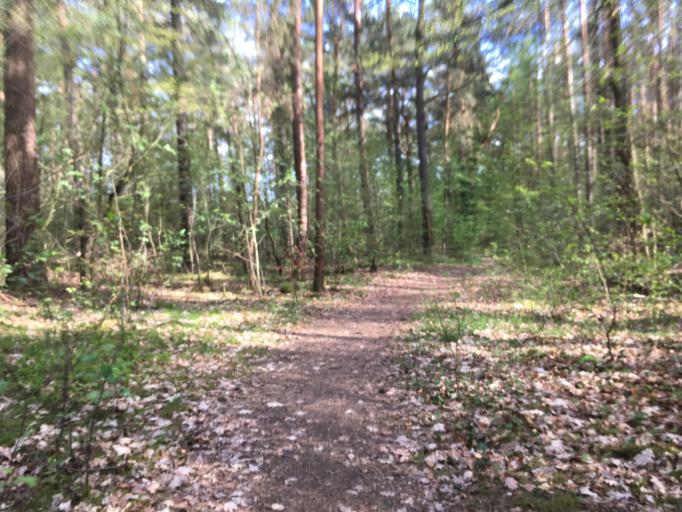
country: DE
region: Brandenburg
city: Bernau bei Berlin
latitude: 52.7056
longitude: 13.5790
